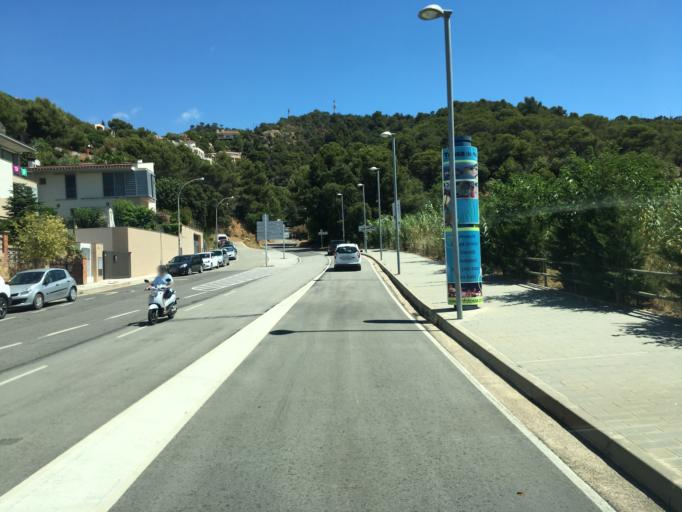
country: ES
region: Catalonia
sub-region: Provincia de Girona
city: Tossa de Mar
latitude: 41.7253
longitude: 2.9332
